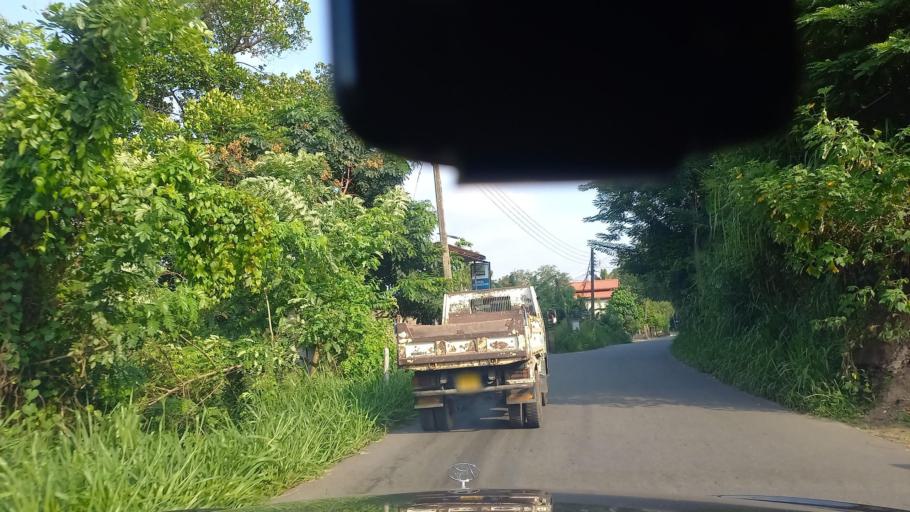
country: LK
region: Central
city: Kandy
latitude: 7.2393
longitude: 80.6007
